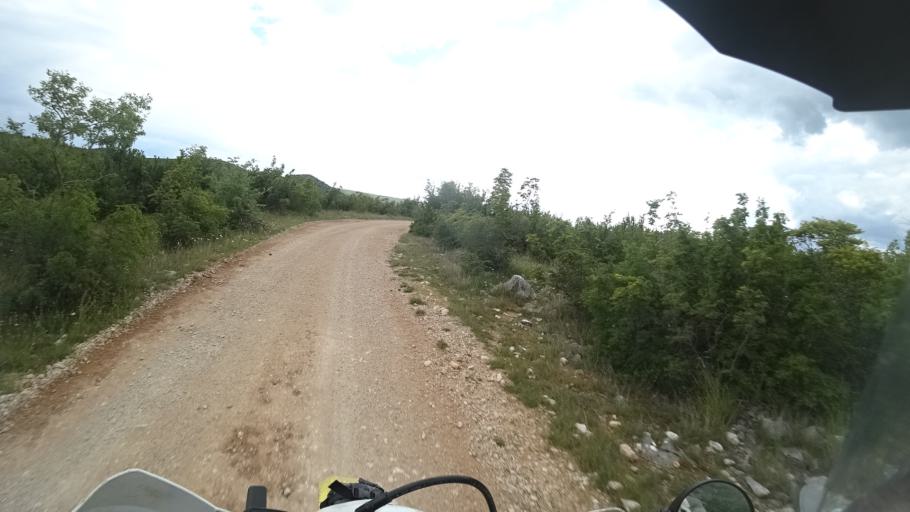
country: HR
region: Sibensko-Kniniska
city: Kistanje
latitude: 44.0981
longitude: 15.9765
